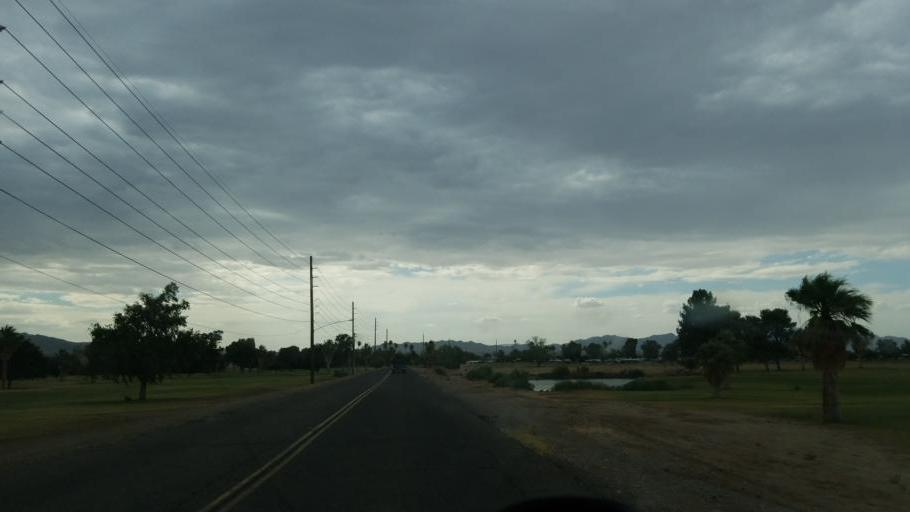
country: US
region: California
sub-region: San Bernardino County
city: Needles
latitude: 34.8436
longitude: -114.6017
